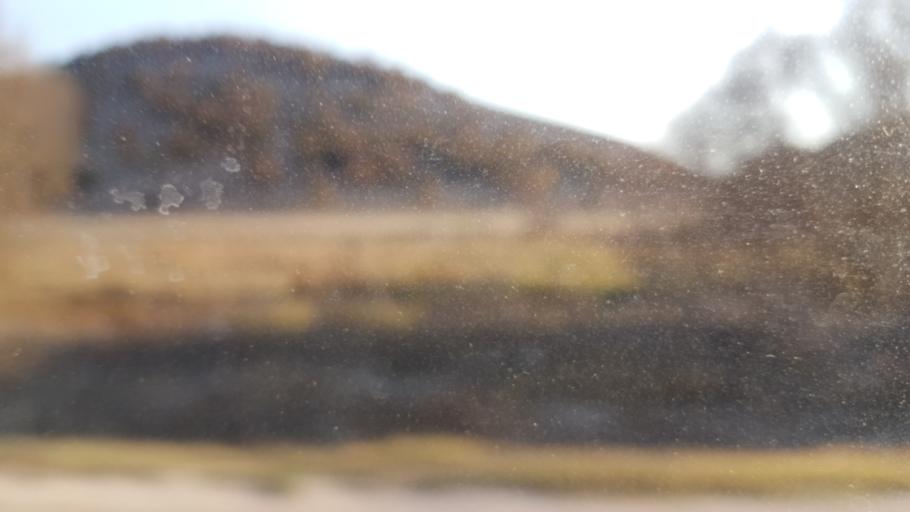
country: TR
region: Eskisehir
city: Kirka
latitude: 39.3572
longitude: 30.5883
